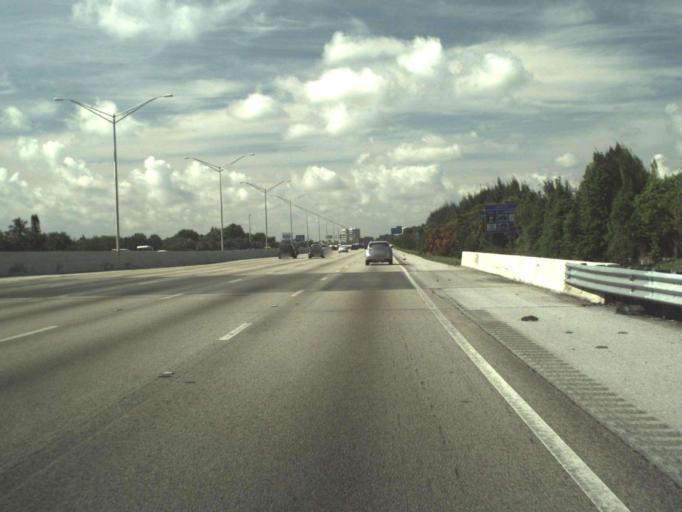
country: US
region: Florida
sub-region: Palm Beach County
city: Schall Circle
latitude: 26.7338
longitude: -80.0913
